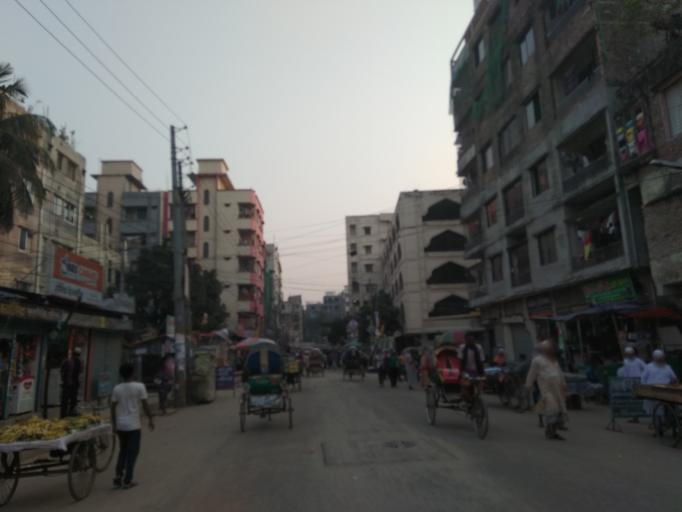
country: BD
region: Dhaka
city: Azimpur
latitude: 23.8115
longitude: 90.3640
